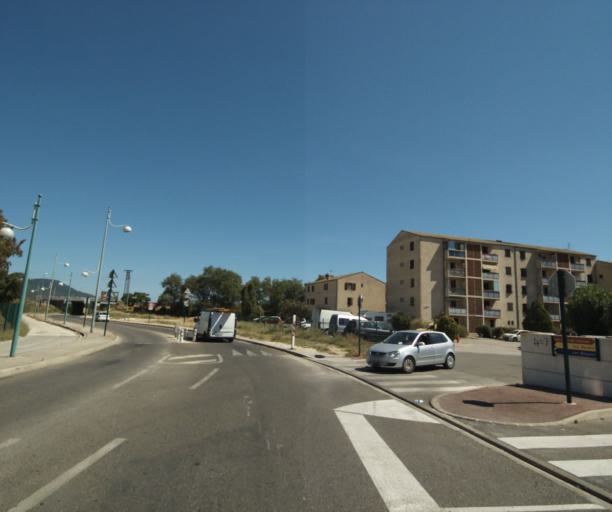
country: FR
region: Provence-Alpes-Cote d'Azur
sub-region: Departement du Var
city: La Garde
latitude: 43.1248
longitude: 6.0172
